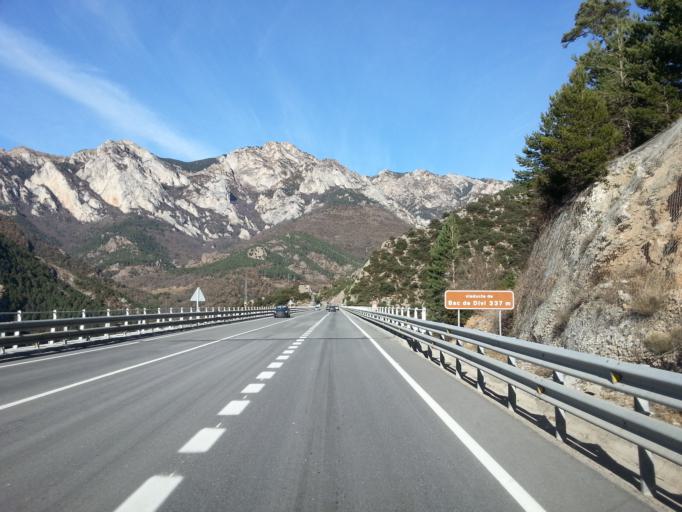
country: ES
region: Catalonia
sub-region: Provincia de Barcelona
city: Baga
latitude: 42.2727
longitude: 1.8538
